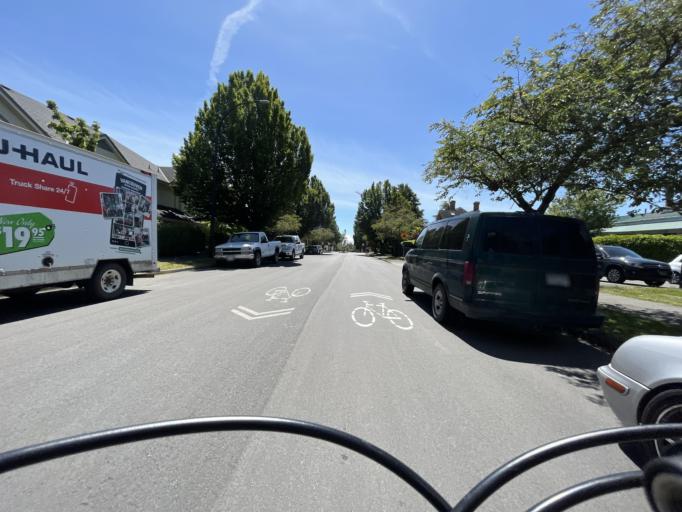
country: CA
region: British Columbia
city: Victoria
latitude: 48.4295
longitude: -123.3559
